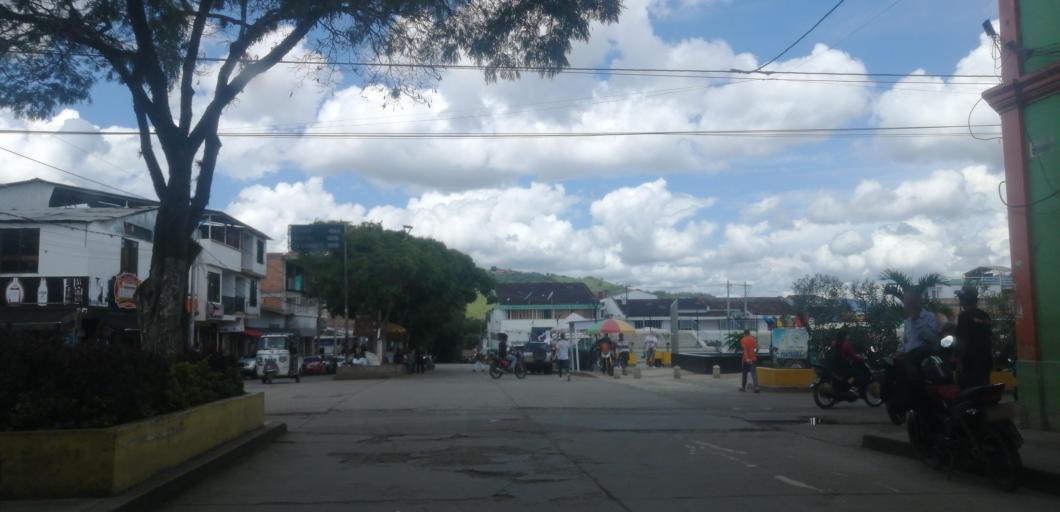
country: CO
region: Valle del Cauca
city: Restrepo
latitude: 3.8214
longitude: -76.5227
